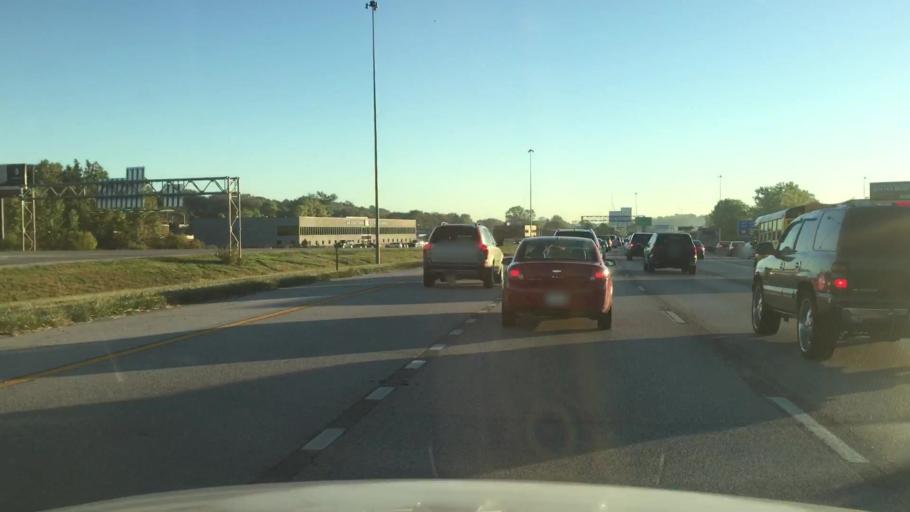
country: US
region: Kansas
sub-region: Johnson County
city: Mission
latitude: 39.0416
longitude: -94.6688
